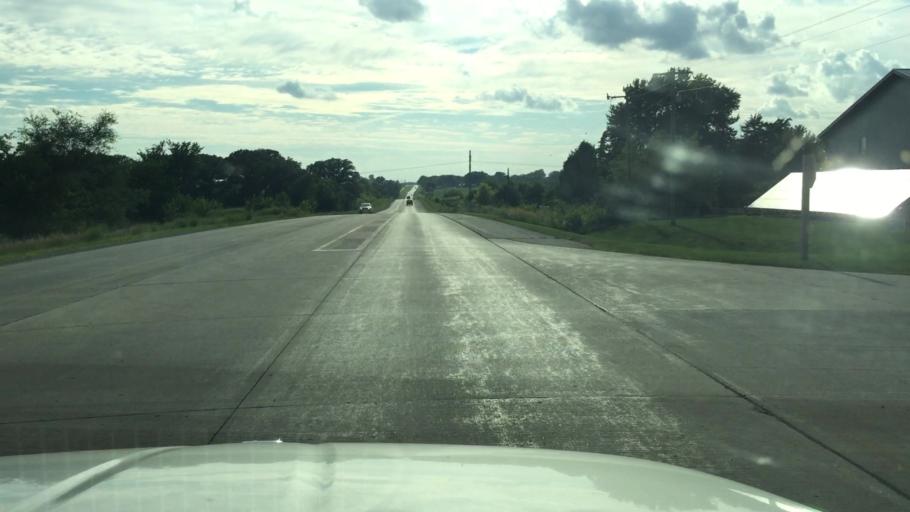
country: US
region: Iowa
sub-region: Johnson County
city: Iowa City
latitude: 41.6711
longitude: -91.4541
